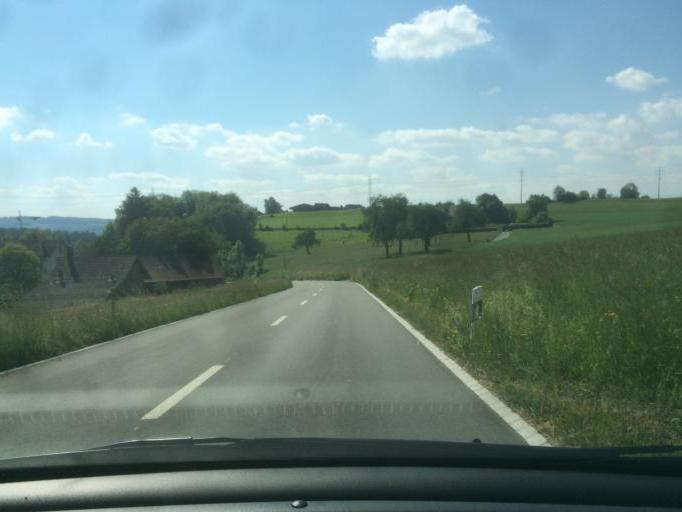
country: CH
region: Zurich
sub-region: Bezirk Uster
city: Uster / Ober-Uster
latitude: 47.3463
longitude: 8.7433
